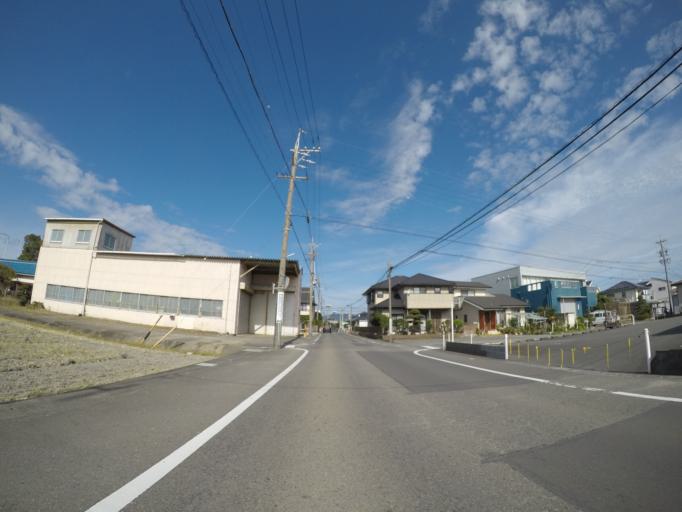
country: JP
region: Shizuoka
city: Fujieda
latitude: 34.8390
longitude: 138.2850
